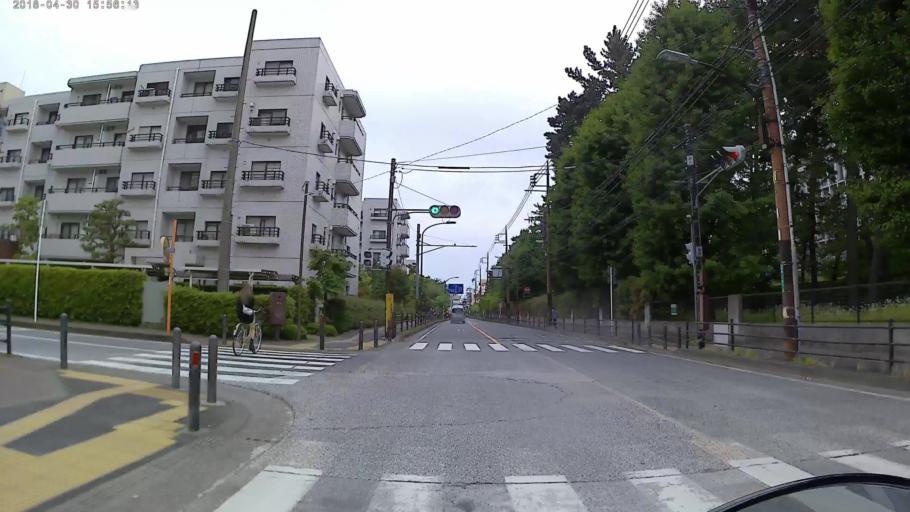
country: JP
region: Tokyo
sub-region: Machida-shi
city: Machida
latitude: 35.5338
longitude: 139.4305
